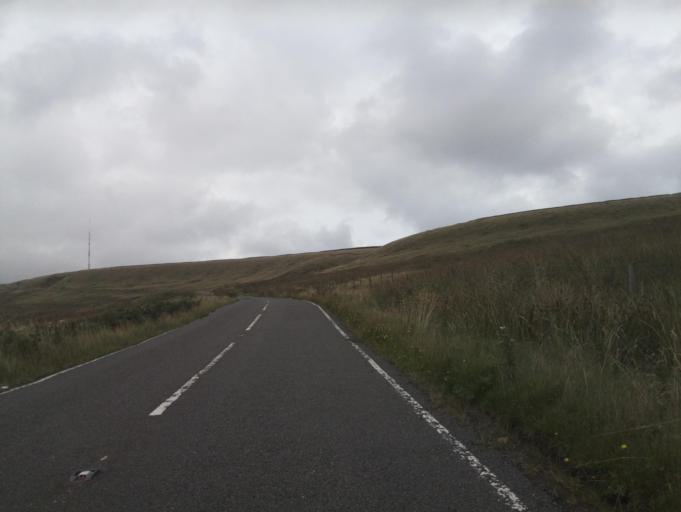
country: GB
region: England
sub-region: Kirklees
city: Meltham
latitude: 53.5186
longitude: -1.8514
